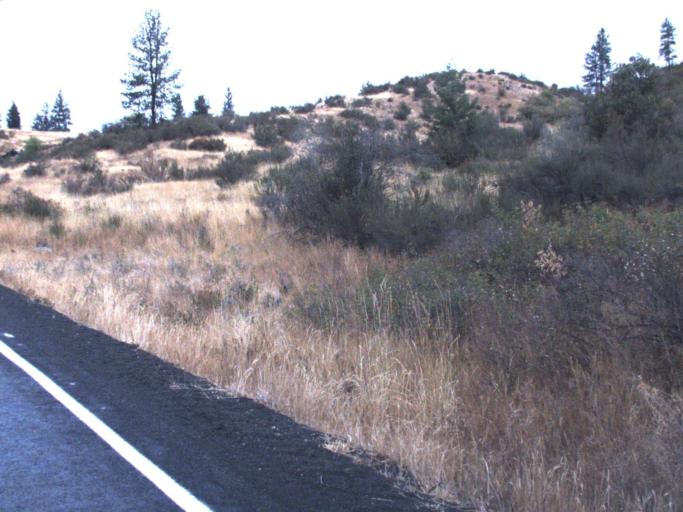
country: US
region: Washington
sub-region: Lincoln County
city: Davenport
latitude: 47.7702
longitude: -117.8922
